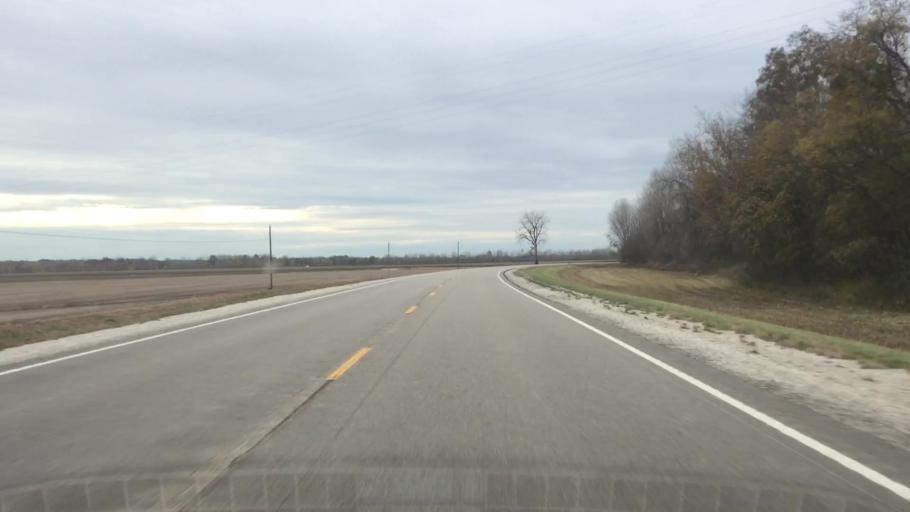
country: US
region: Missouri
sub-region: Callaway County
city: Holts Summit
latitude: 38.5804
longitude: -92.0944
